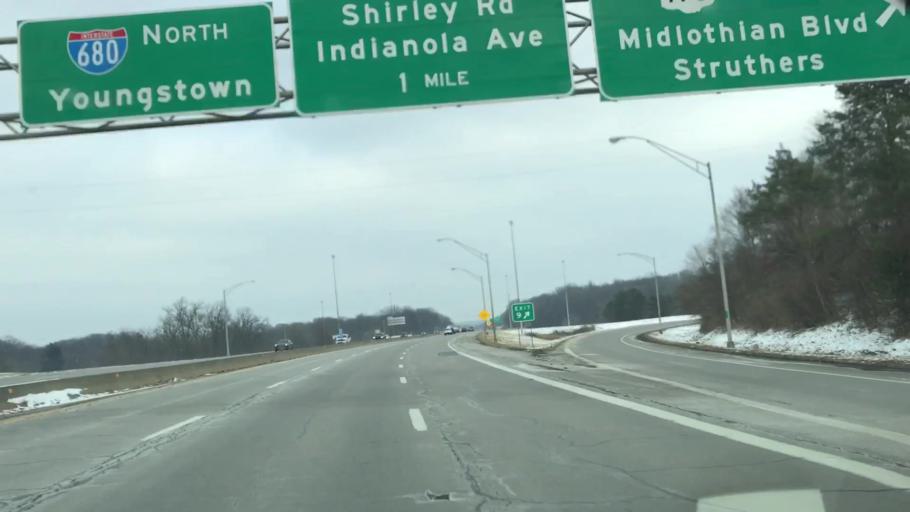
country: US
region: Ohio
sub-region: Mahoning County
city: Struthers
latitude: 41.0574
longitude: -80.6291
